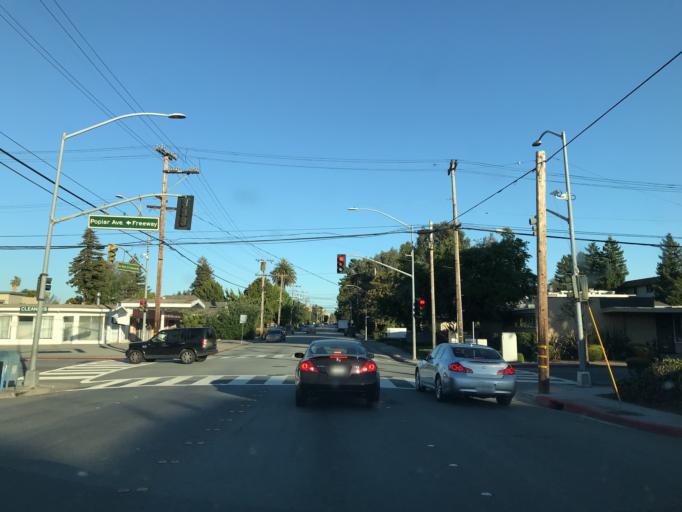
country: US
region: California
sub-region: San Mateo County
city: San Mateo
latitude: 37.5723
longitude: -122.3327
